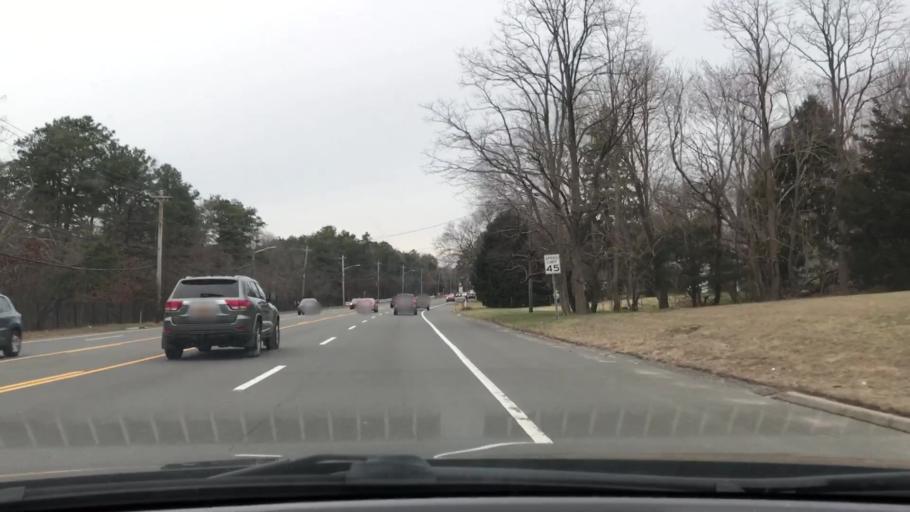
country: US
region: New York
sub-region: Suffolk County
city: Medford
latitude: 40.8074
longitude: -73.0191
